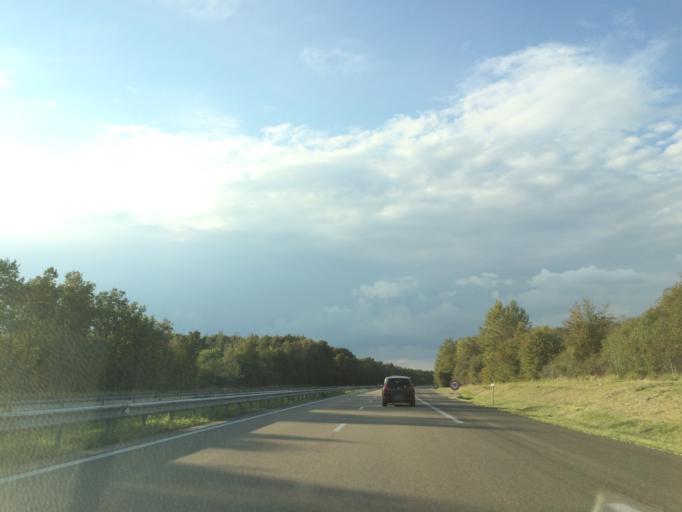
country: FR
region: Bourgogne
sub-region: Departement de l'Yonne
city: Cheroy
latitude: 48.1164
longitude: 2.9833
